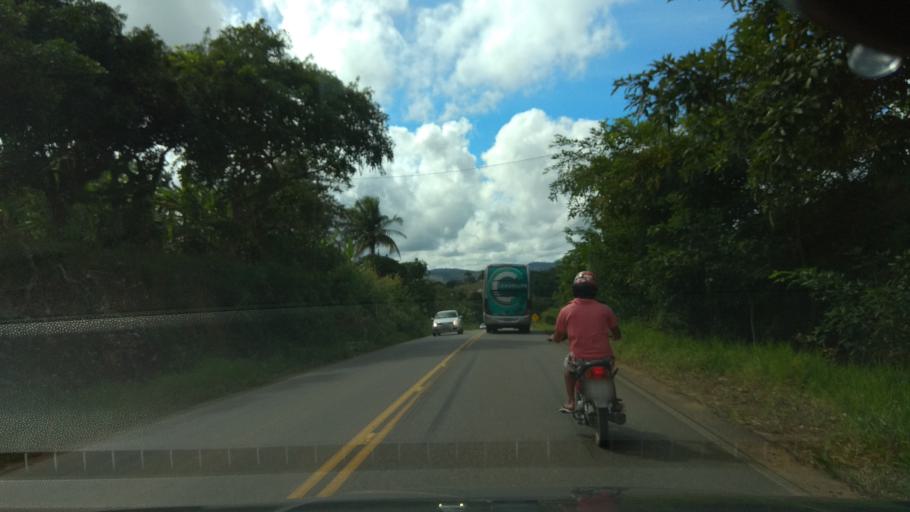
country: BR
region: Bahia
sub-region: Mutuipe
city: Mutuipe
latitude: -13.2128
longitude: -39.4793
